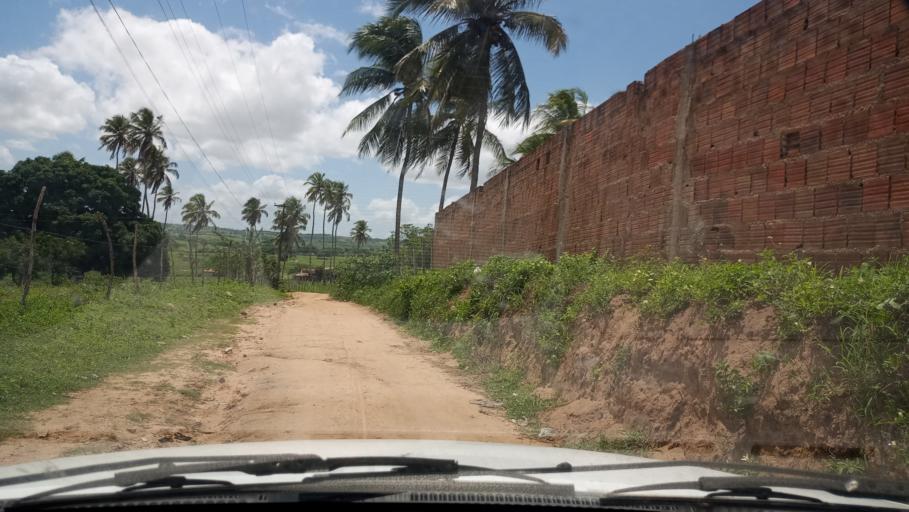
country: BR
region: Rio Grande do Norte
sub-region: Brejinho
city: Brejinho
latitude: -6.2630
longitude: -35.3744
